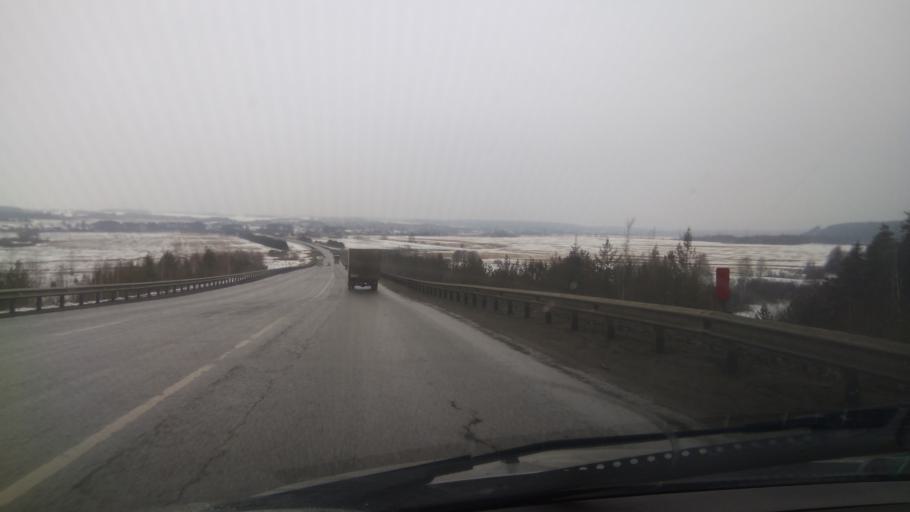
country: RU
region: Perm
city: Kungur
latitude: 57.3552
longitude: 56.9337
